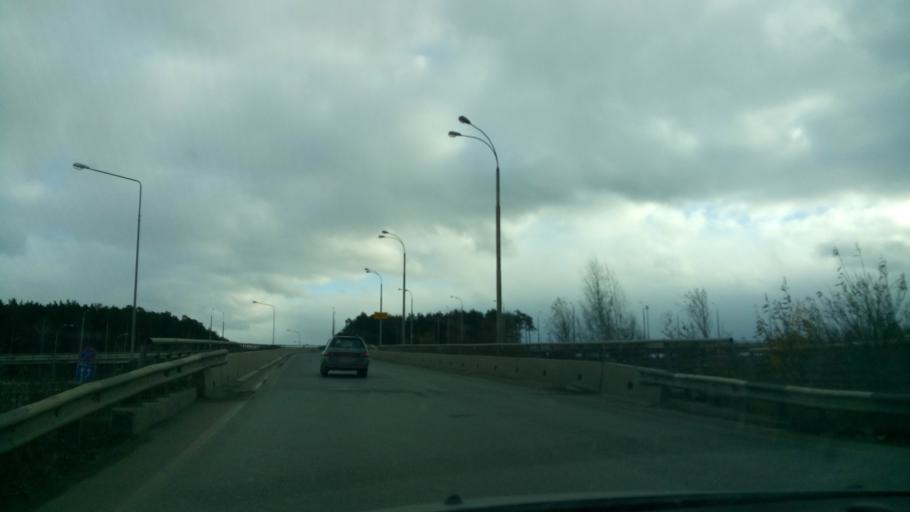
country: RU
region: Sverdlovsk
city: Shuvakish
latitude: 56.8941
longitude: 60.5317
